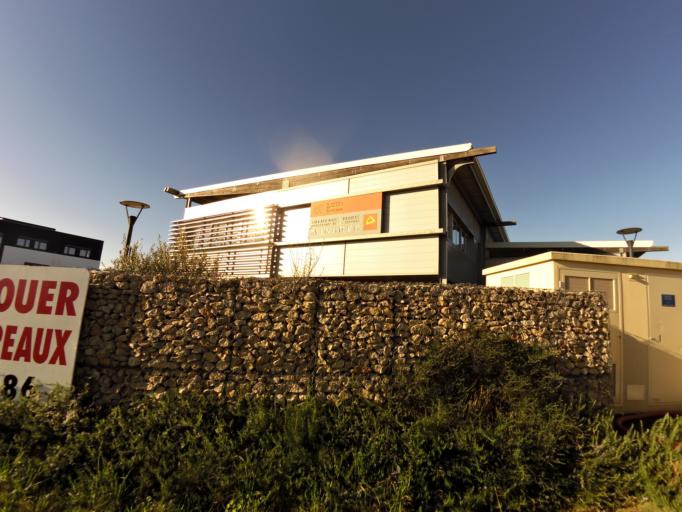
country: FR
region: Languedoc-Roussillon
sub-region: Departement de l'Herault
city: Vendargues
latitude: 43.6705
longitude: 3.9717
